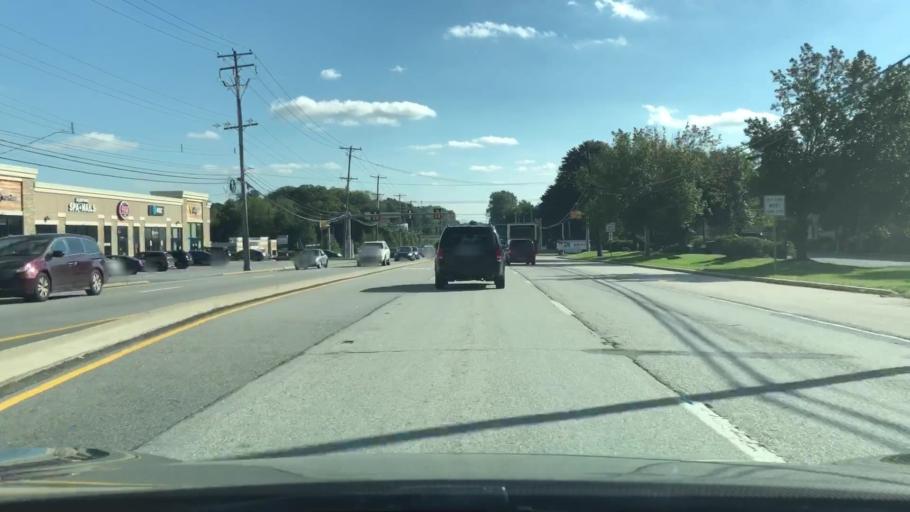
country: US
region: Pennsylvania
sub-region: Delaware County
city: Chester Heights
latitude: 39.8770
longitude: -75.5450
